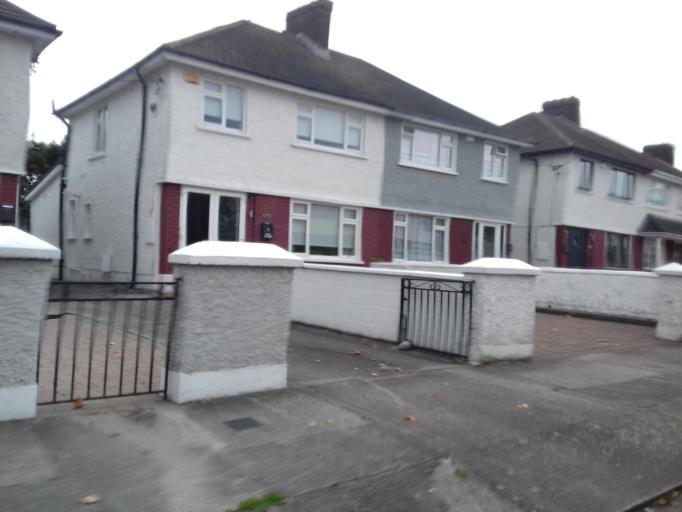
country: IE
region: Leinster
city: Artane
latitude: 53.3798
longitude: -6.2251
